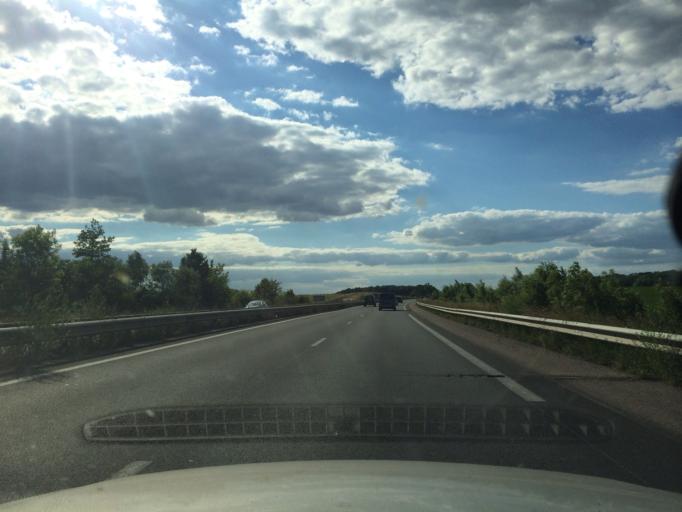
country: FR
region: Lorraine
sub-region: Departement de Meurthe-et-Moselle
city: Damelevieres
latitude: 48.5946
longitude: 6.3982
